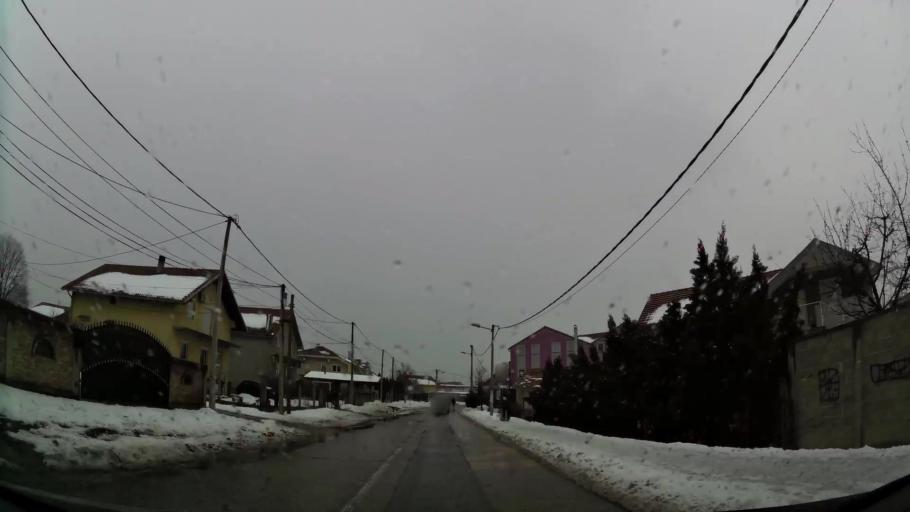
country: RS
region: Central Serbia
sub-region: Belgrade
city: Zemun
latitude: 44.8469
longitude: 20.3565
